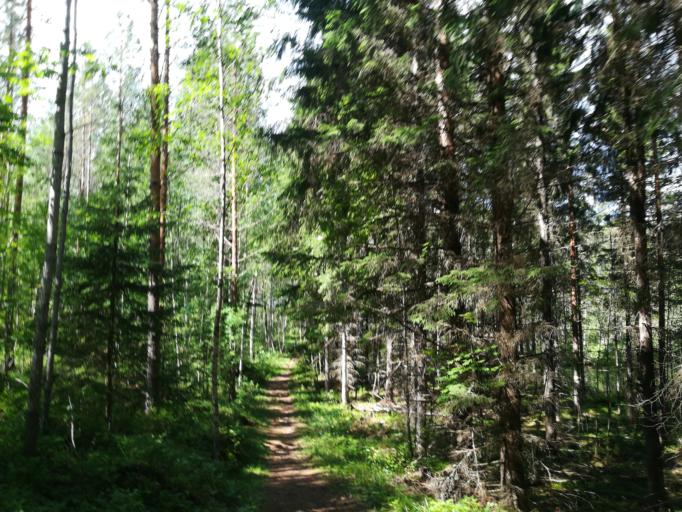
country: FI
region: Southern Savonia
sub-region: Mikkeli
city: Hirvensalmi
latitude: 61.6275
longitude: 26.7636
